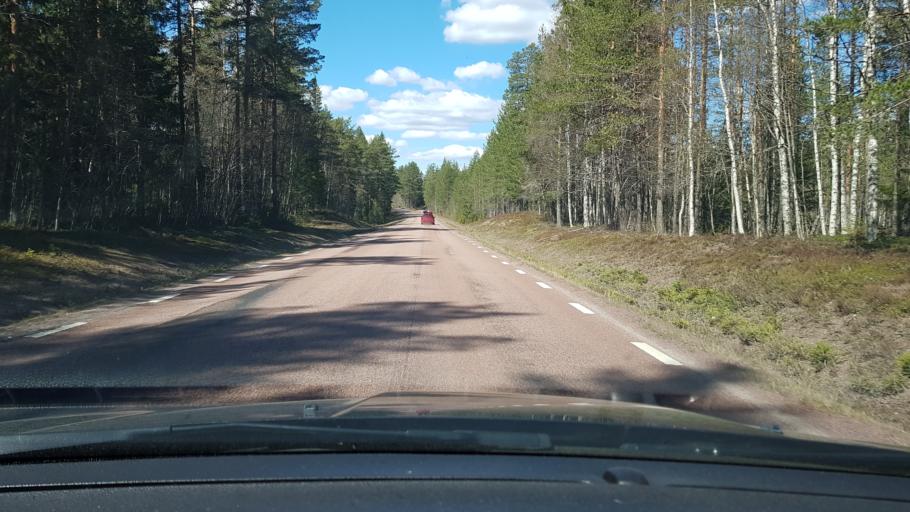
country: SE
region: Dalarna
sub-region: Alvdalens Kommun
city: AElvdalen
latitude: 61.1256
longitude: 14.0284
